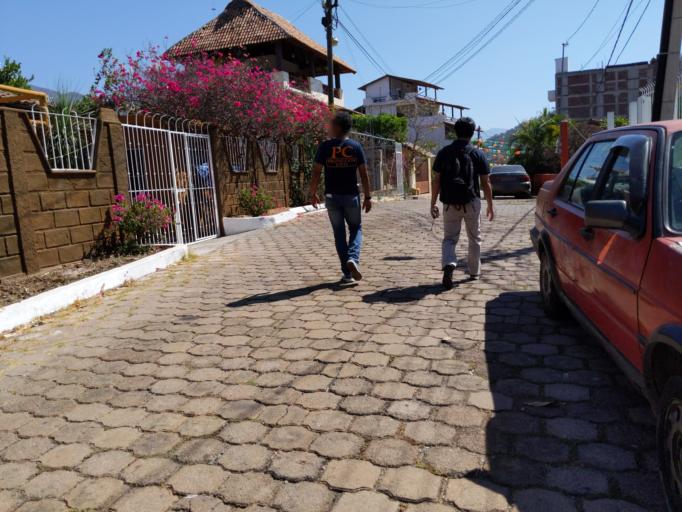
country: MX
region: Guerrero
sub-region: Zihuatanejo de Azueta
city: Ixtapa-Zihuatanejo
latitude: 17.6398
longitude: -101.5535
